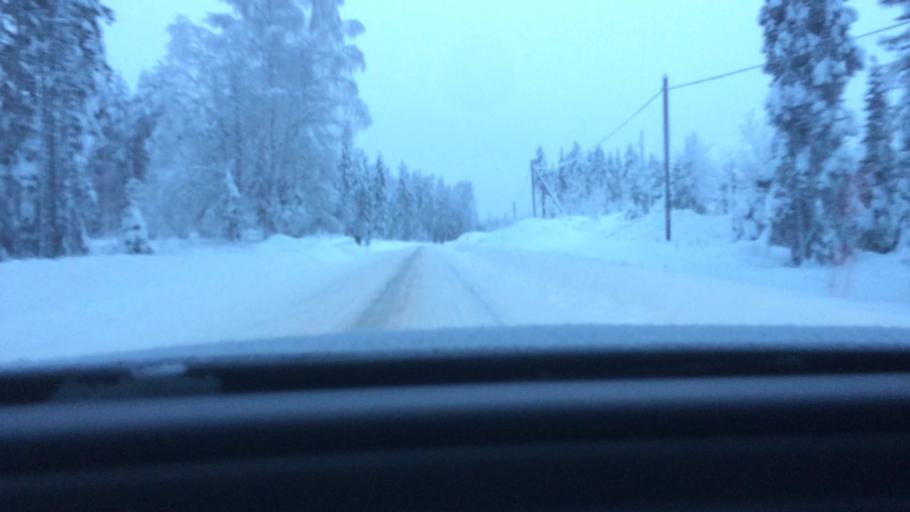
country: SE
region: Gaevleborg
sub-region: Ljusdals Kommun
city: Farila
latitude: 61.7696
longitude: 15.1652
